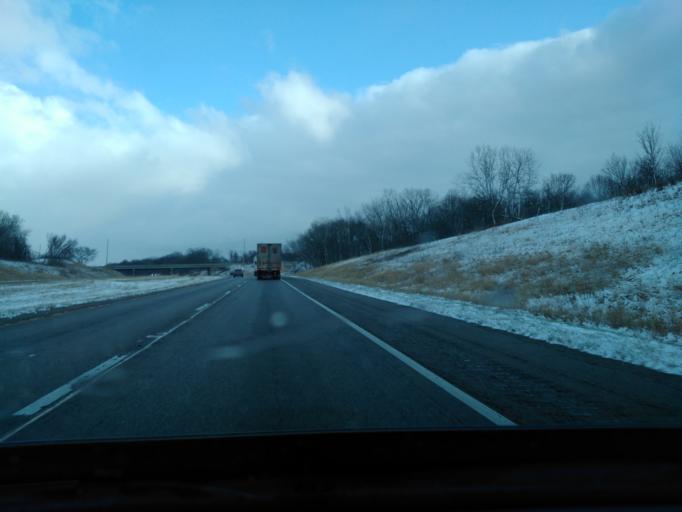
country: US
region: Illinois
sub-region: Bond County
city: Greenville
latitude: 38.8329
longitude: -89.5204
